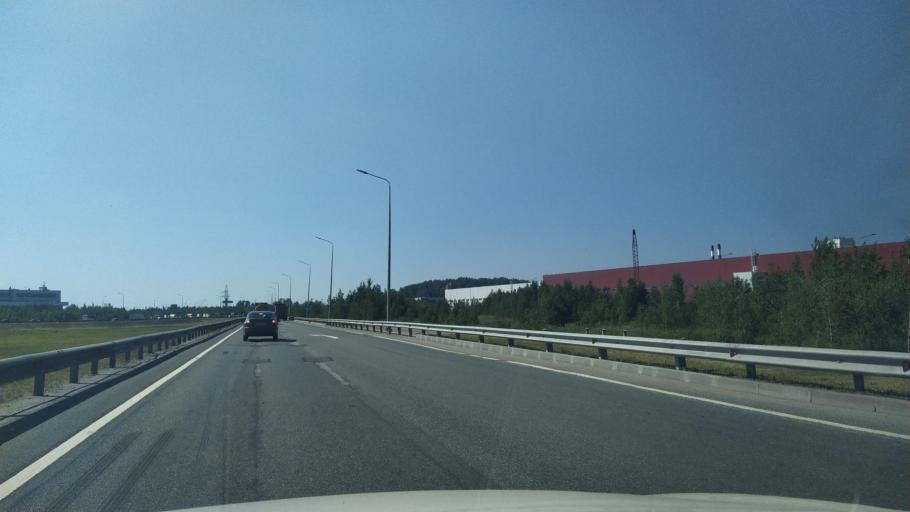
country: RU
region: St.-Petersburg
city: Pargolovo
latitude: 60.1000
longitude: 30.2698
